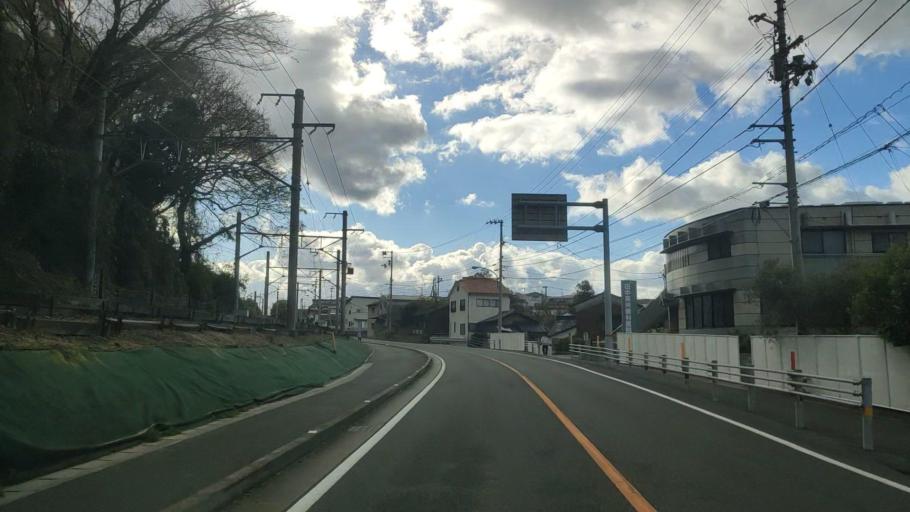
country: JP
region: Ehime
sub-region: Shikoku-chuo Shi
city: Matsuyama
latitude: 33.8811
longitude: 132.7020
